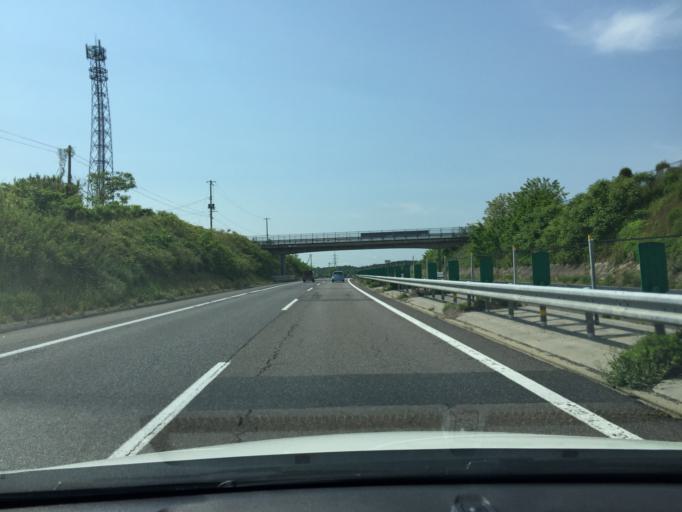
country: JP
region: Fukushima
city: Sukagawa
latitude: 37.3367
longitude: 140.3367
